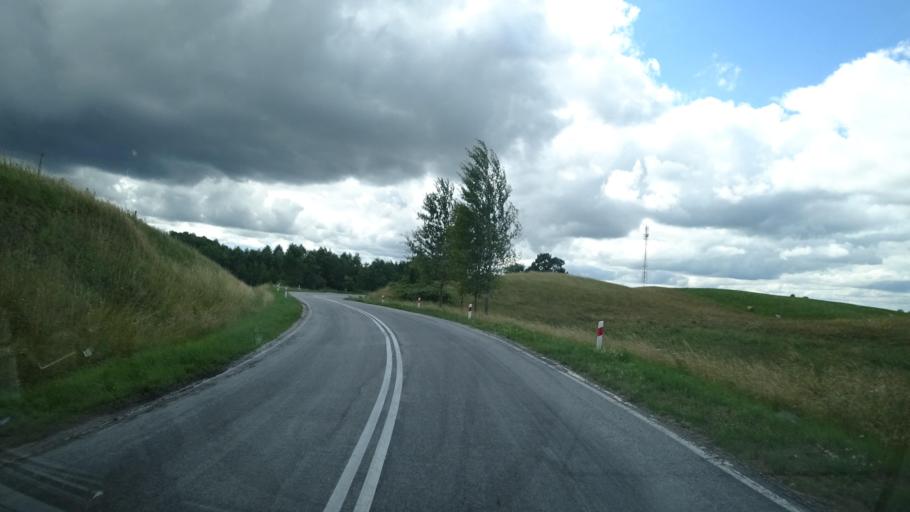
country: PL
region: Warmian-Masurian Voivodeship
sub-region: Powiat goldapski
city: Goldap
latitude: 54.2145
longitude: 22.2197
